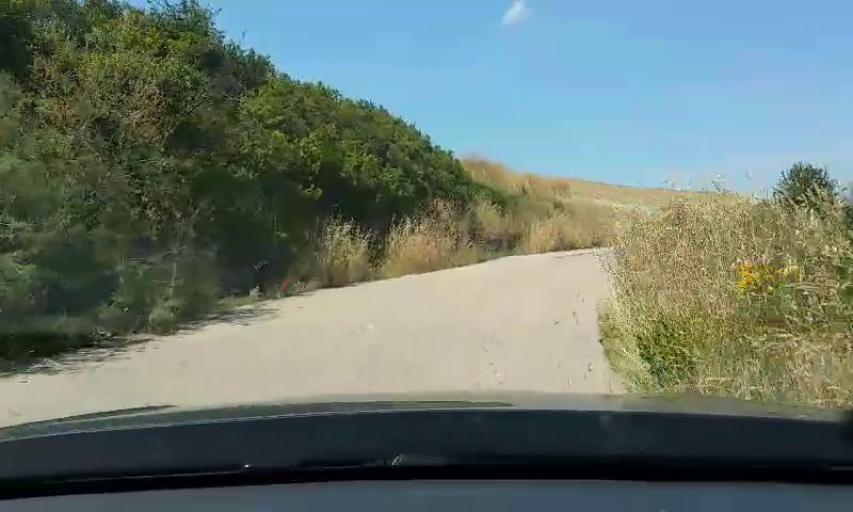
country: IT
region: Molise
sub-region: Provincia di Campobasso
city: Montecilfone
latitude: 41.9236
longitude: 14.8496
